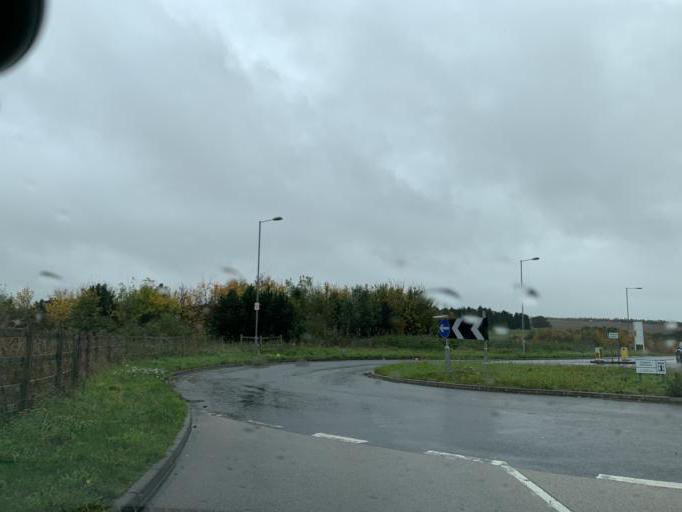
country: GB
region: England
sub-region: Wiltshire
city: Amesbury
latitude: 51.1571
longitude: -1.7644
